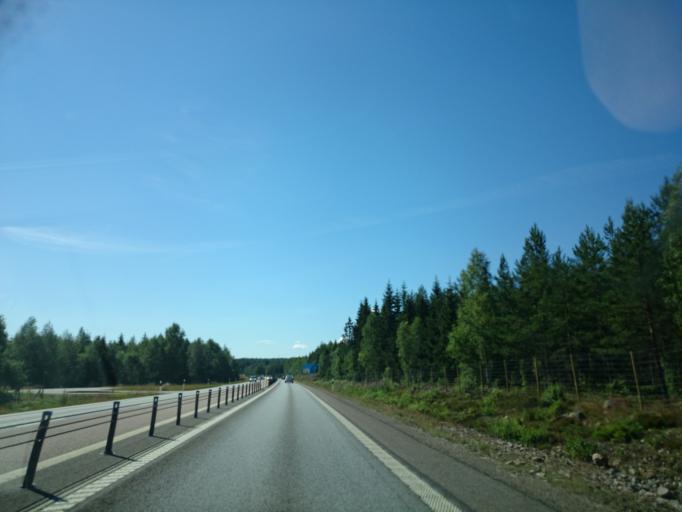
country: SE
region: Gaevleborg
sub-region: Gavle Kommun
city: Norrsundet
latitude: 60.9094
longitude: 17.0143
